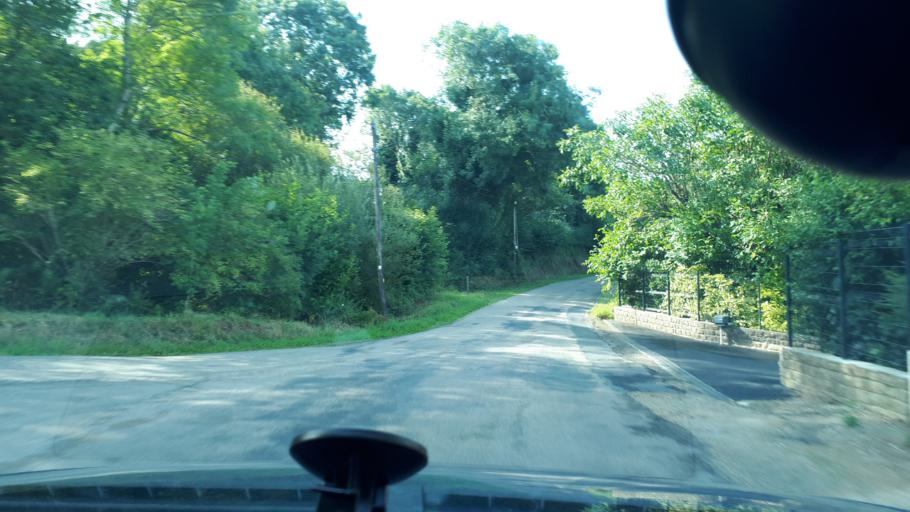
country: FR
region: Brittany
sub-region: Departement du Finistere
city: Pouldreuzic
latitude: 47.9712
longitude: -4.3673
